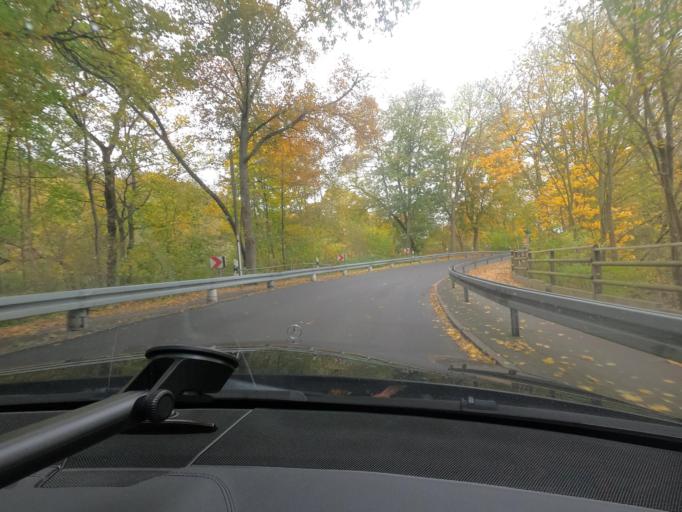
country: DE
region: North Rhine-Westphalia
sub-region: Regierungsbezirk Arnsberg
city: Mohnesee
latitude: 51.4882
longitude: 8.0947
